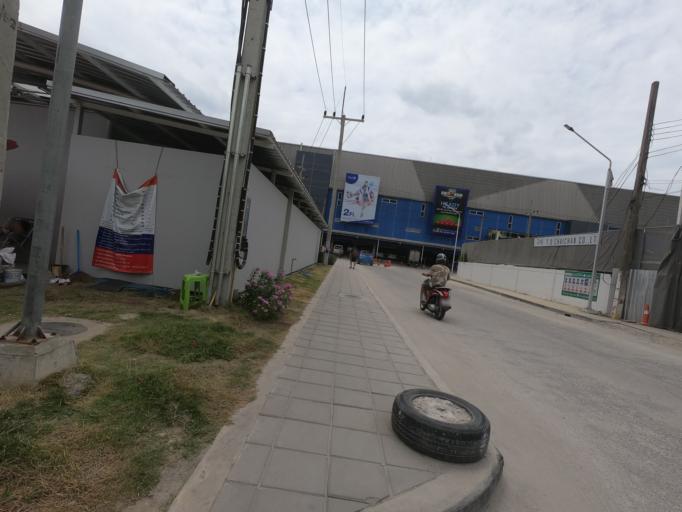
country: TH
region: Bangkok
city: Sai Mai
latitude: 13.9530
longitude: 100.6513
